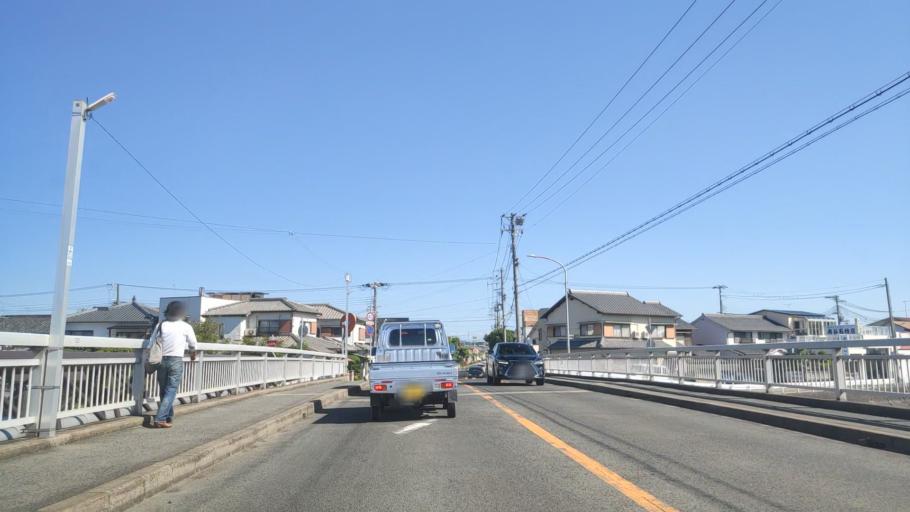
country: JP
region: Hyogo
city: Akashi
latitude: 34.6580
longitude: 134.9897
